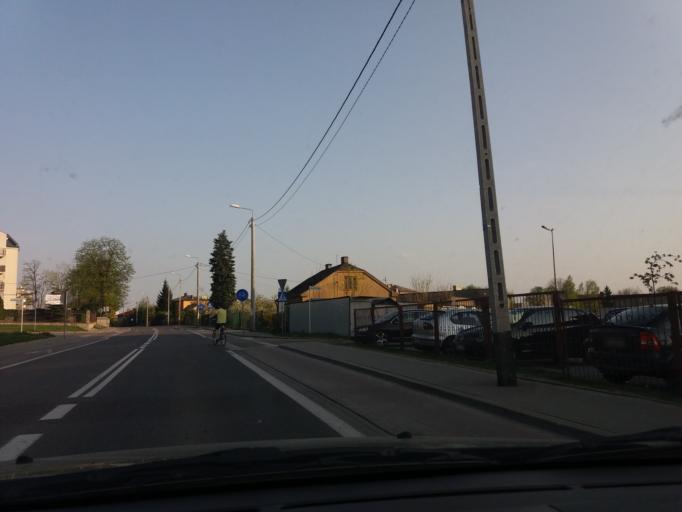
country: PL
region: Masovian Voivodeship
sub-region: Powiat mlawski
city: Mlawa
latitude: 53.1255
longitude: 20.3587
